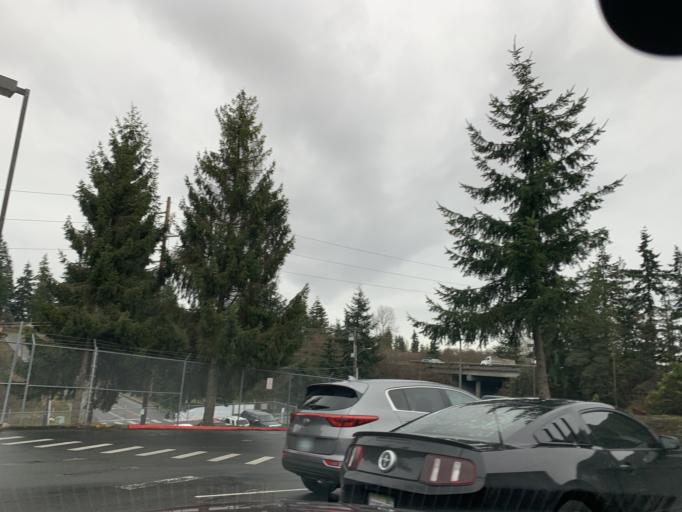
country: US
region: Washington
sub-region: Snohomish County
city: Mukilteo
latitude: 47.9244
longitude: -122.2413
